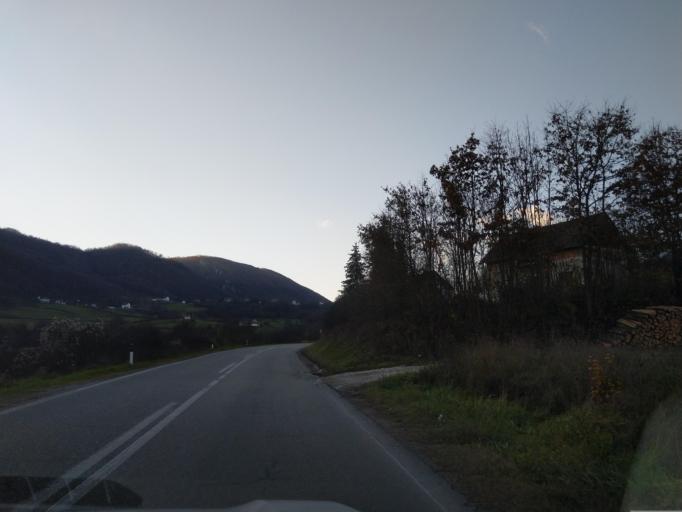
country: RS
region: Central Serbia
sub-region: Zlatiborski Okrug
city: Kosjeric
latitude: 43.9777
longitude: 19.9505
